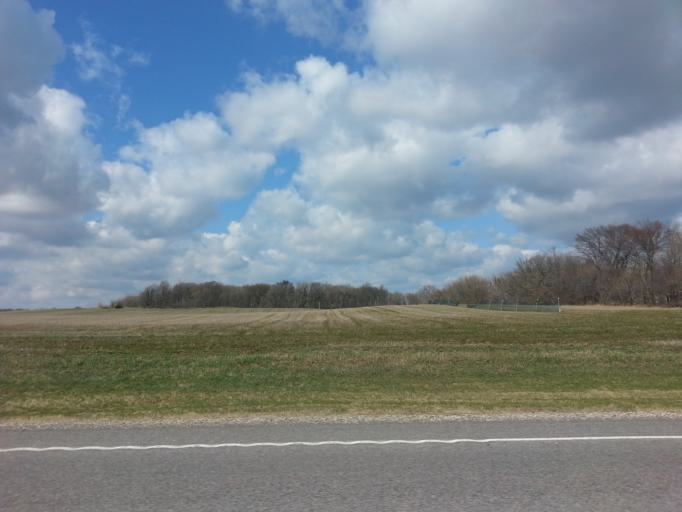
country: US
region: Minnesota
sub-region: Dodge County
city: Mantorville
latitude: 44.0798
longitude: -92.7143
